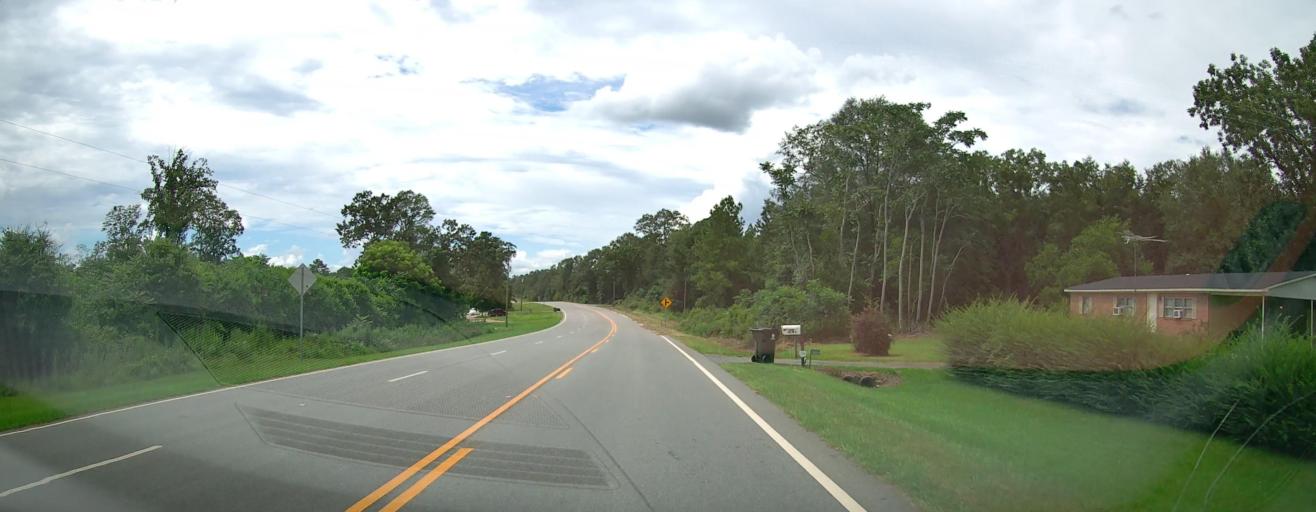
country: US
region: Georgia
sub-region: Macon County
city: Oglethorpe
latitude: 32.2811
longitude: -84.1440
